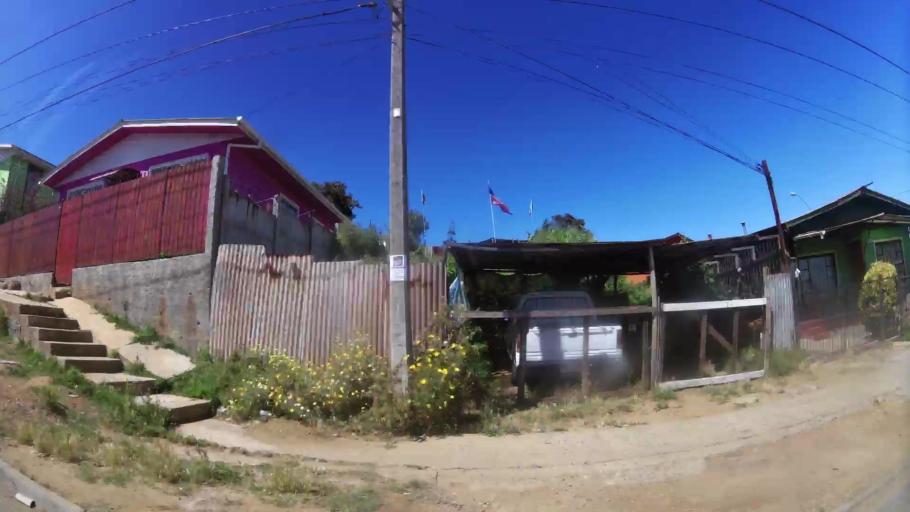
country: CL
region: Valparaiso
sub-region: Provincia de Valparaiso
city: Vina del Mar
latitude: -33.0565
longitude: -71.5794
